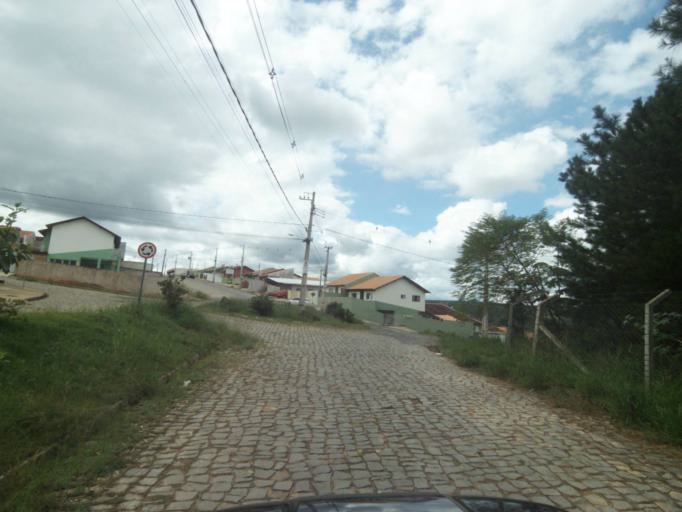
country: BR
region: Parana
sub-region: Telemaco Borba
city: Telemaco Borba
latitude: -24.3100
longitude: -50.6348
